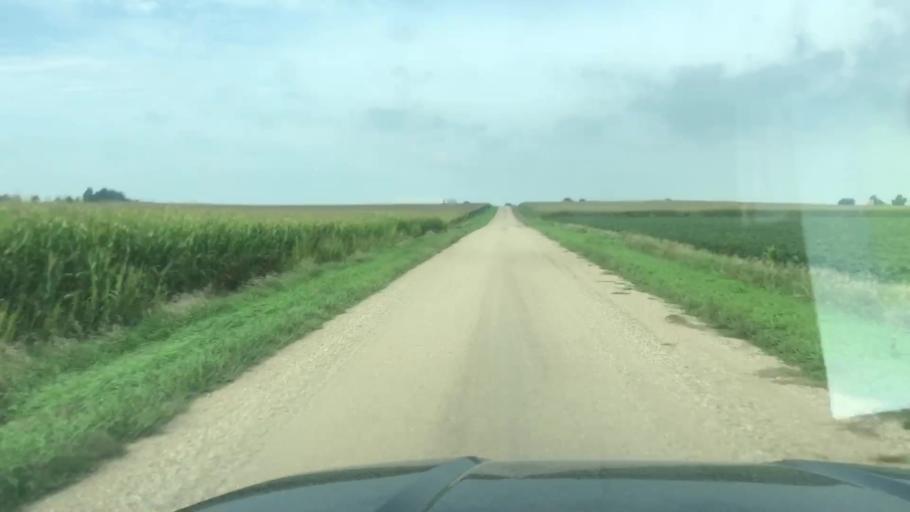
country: US
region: Iowa
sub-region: Lyon County
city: George
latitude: 43.2724
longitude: -95.9874
